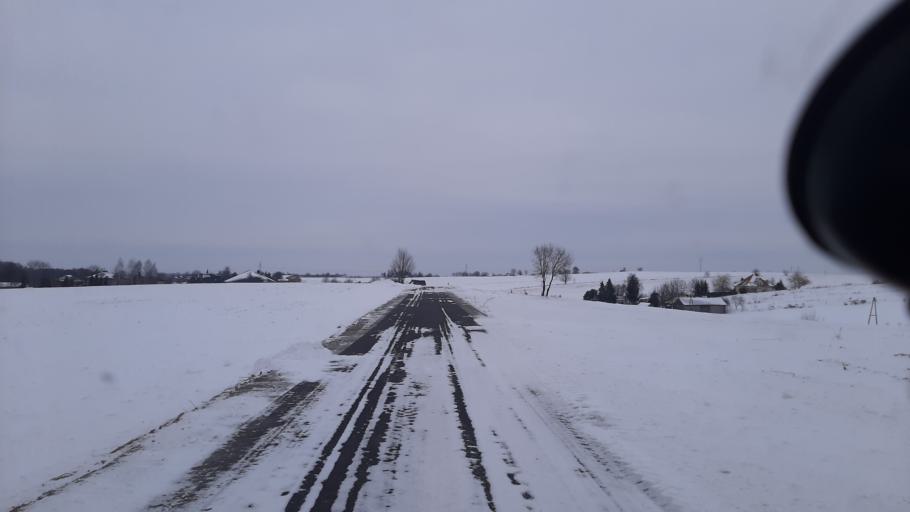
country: PL
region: Lublin Voivodeship
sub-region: Powiat lubelski
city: Garbow
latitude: 51.3358
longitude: 22.2924
